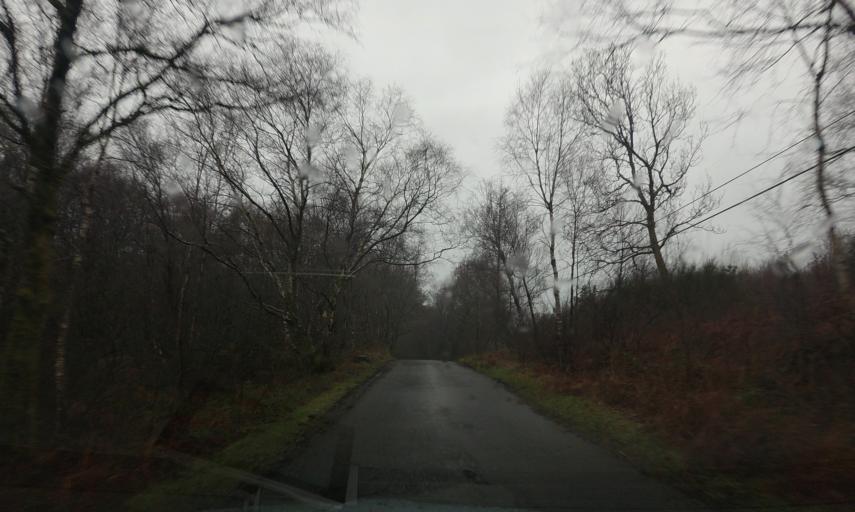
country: GB
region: Scotland
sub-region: West Dunbartonshire
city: Balloch
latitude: 56.1418
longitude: -4.6342
